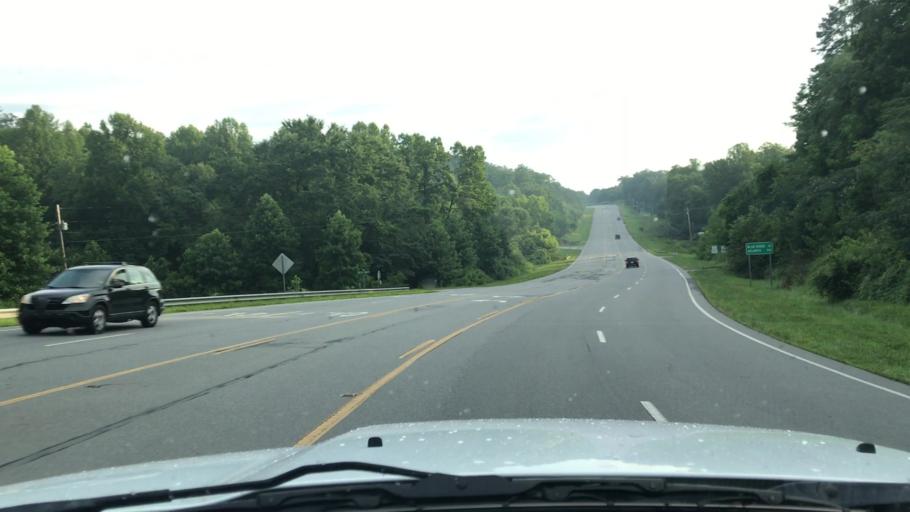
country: US
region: North Carolina
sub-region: Cherokee County
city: Murphy
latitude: 35.0262
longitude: -84.1118
